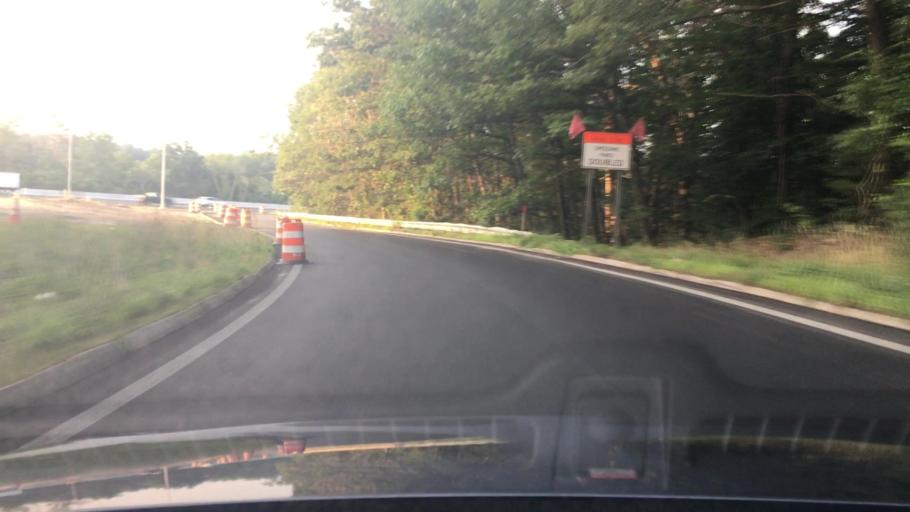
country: US
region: Massachusetts
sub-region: Essex County
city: Amesbury
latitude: 42.8435
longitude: -70.9059
